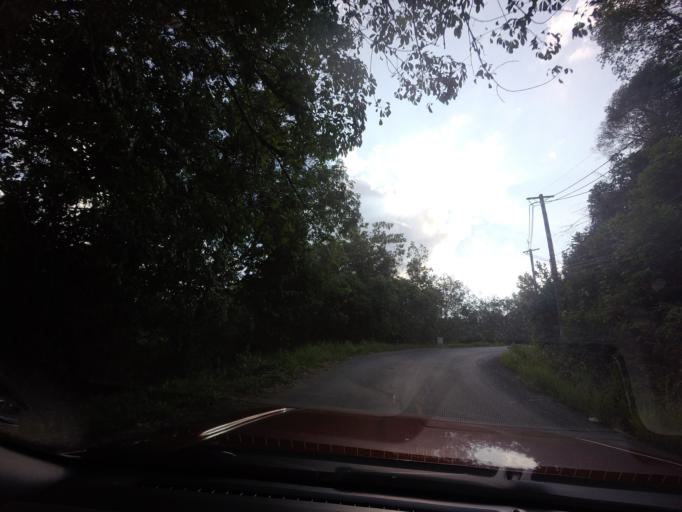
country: TH
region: Yala
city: Than To
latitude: 6.1432
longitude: 101.2862
